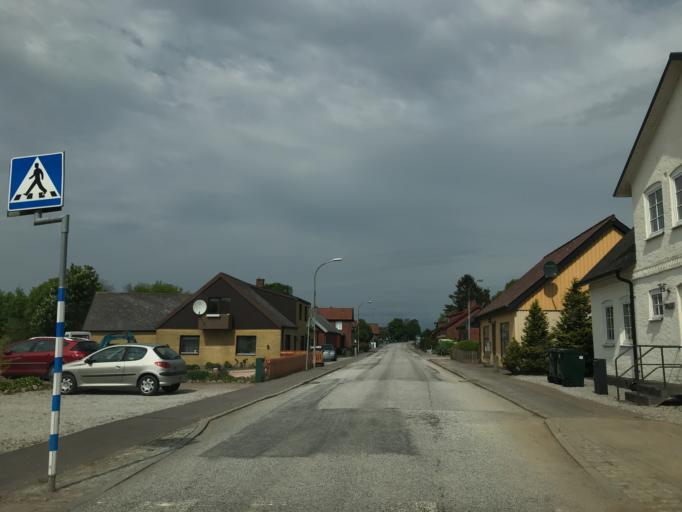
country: SE
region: Skane
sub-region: Svalovs Kommun
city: Svaloev
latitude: 55.8659
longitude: 13.1524
